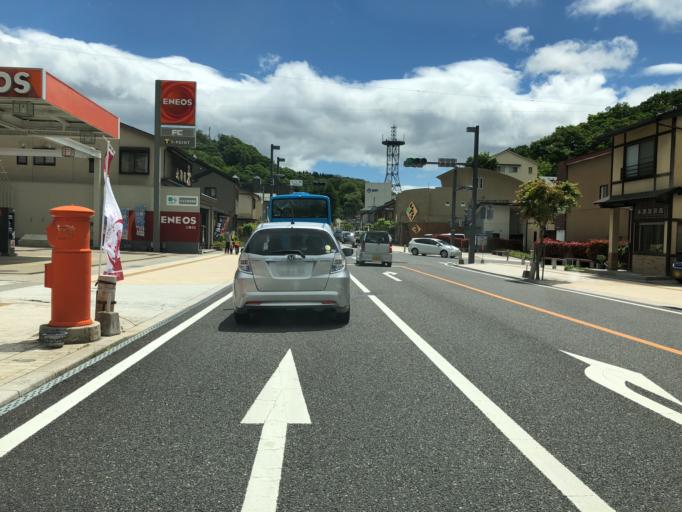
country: JP
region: Fukushima
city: Miharu
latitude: 37.4426
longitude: 140.4887
